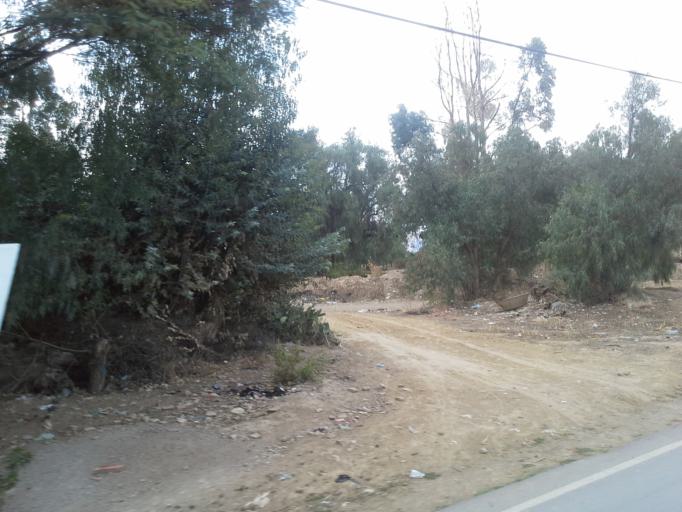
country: BO
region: Cochabamba
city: Tarata
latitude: -17.5802
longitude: -66.0155
